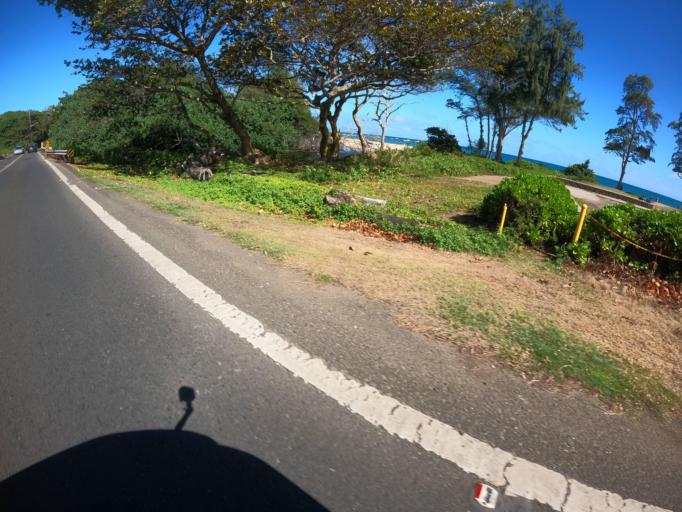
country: US
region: Hawaii
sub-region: Honolulu County
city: La'ie
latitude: 21.6323
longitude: -157.9214
